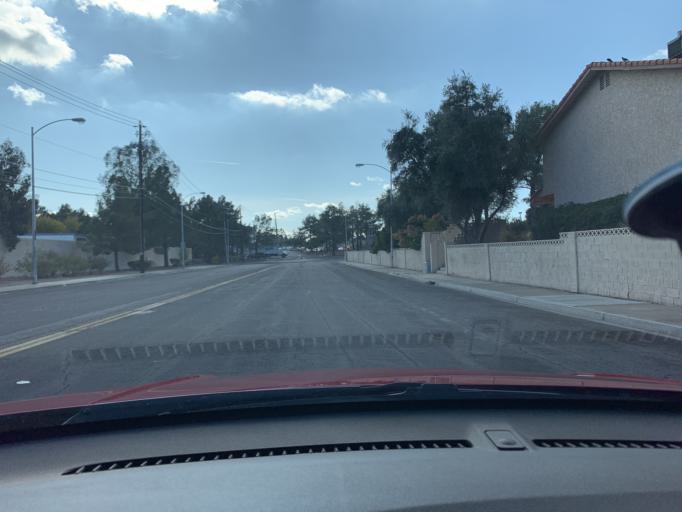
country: US
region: Nevada
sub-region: Clark County
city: Winchester
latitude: 36.1199
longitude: -115.1009
